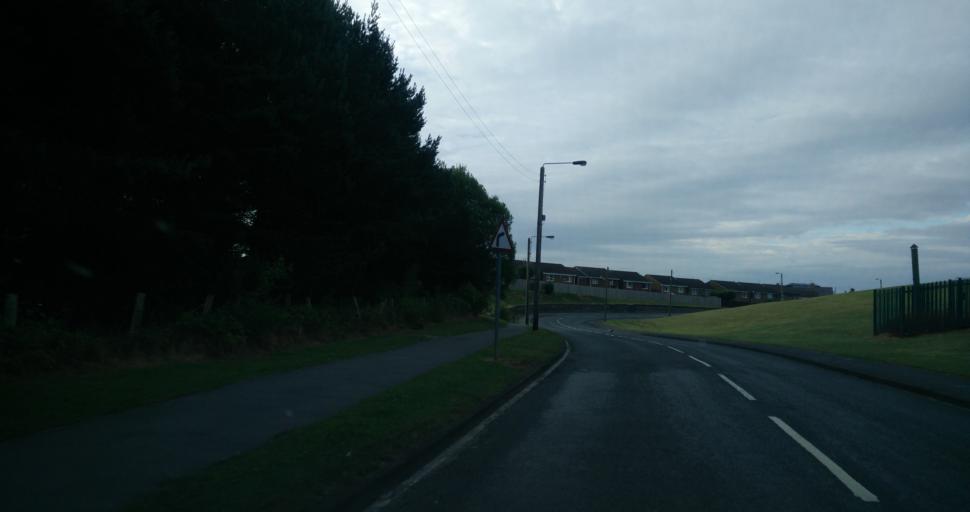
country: GB
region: England
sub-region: County Durham
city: Crook
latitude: 54.7200
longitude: -1.7487
